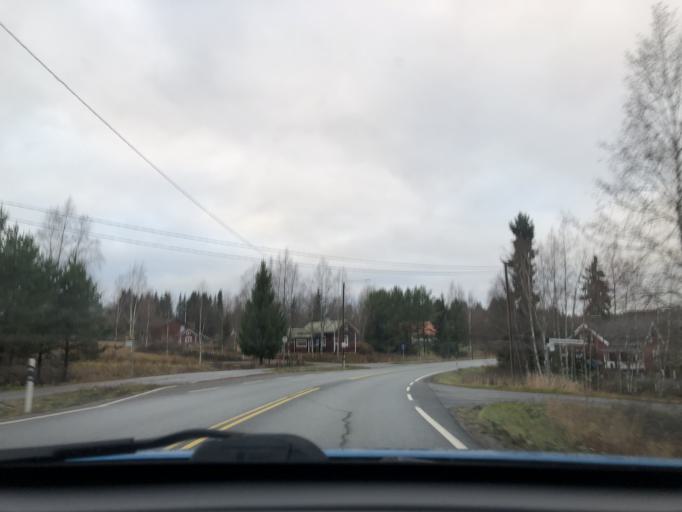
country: FI
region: Pirkanmaa
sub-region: Tampere
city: Kangasala
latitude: 61.5150
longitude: 24.0348
